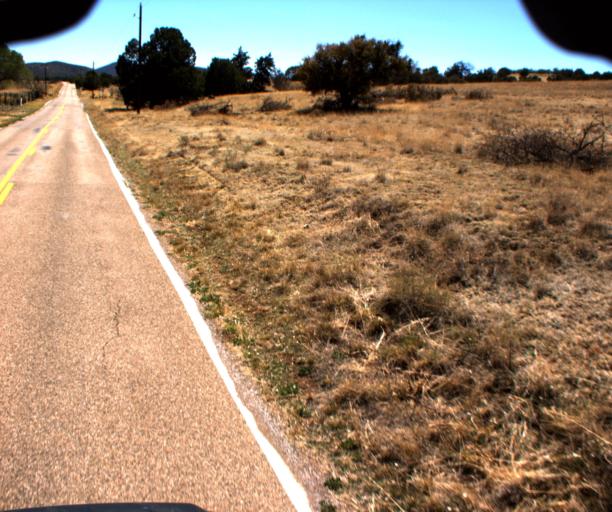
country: US
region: Arizona
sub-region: Cochise County
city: Huachuca City
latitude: 31.5526
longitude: -110.5290
